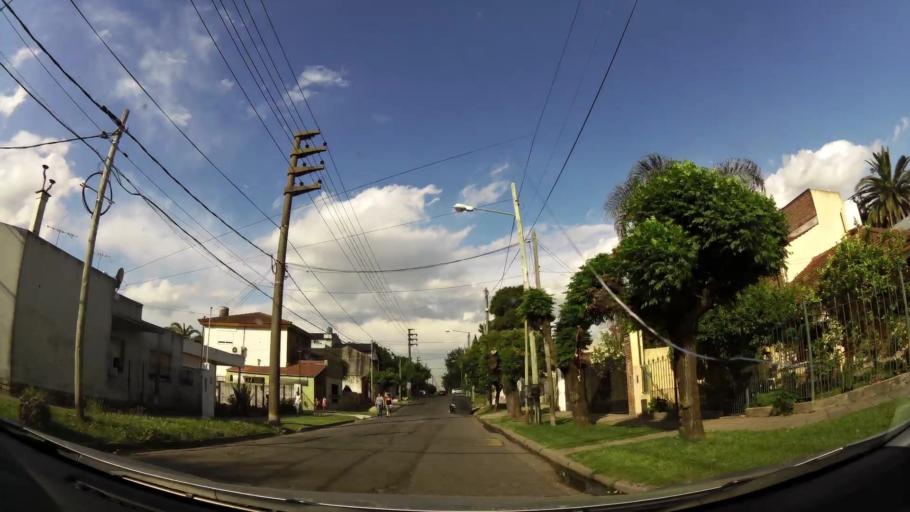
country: AR
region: Buenos Aires
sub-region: Partido de Tigre
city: Tigre
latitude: -34.4707
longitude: -58.6482
